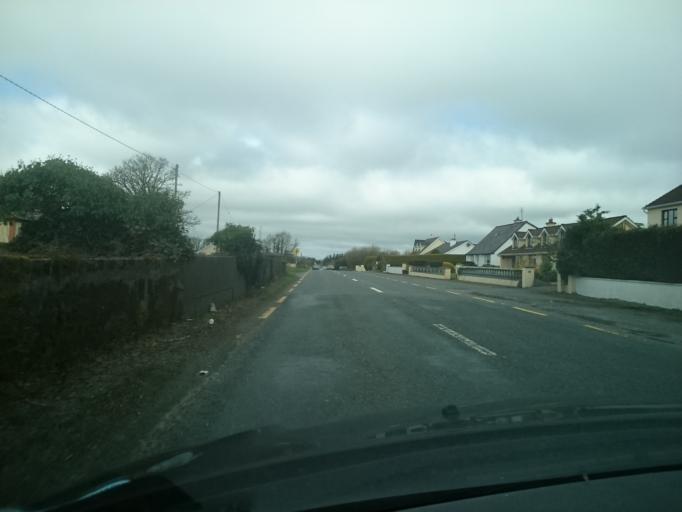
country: IE
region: Connaught
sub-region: Maigh Eo
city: Claremorris
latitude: 53.7503
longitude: -9.0277
